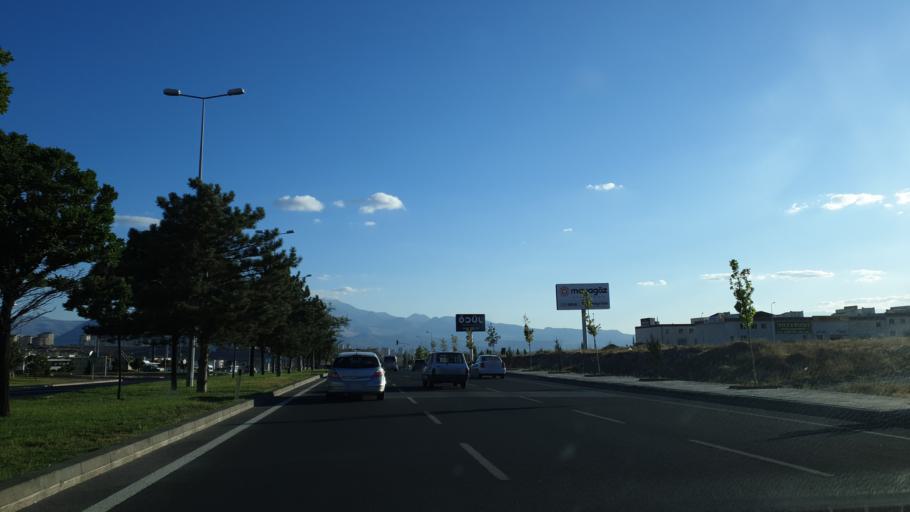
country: TR
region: Kayseri
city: Kocasinan
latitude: 38.7785
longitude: 35.5748
